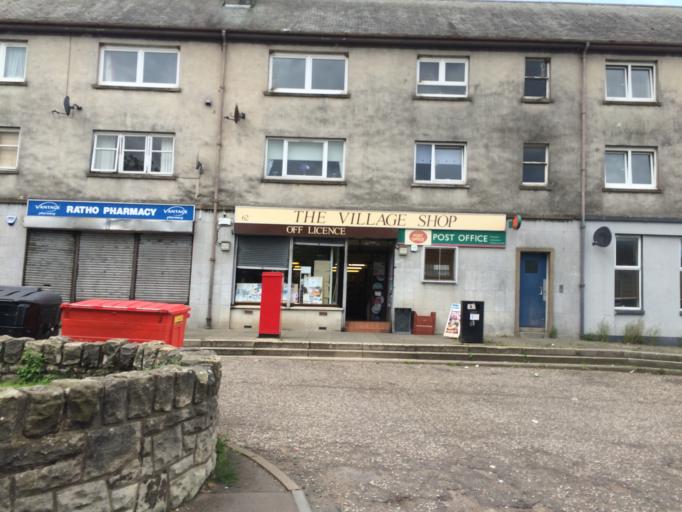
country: GB
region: Scotland
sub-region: Edinburgh
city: Ratho
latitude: 55.9218
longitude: -3.3816
